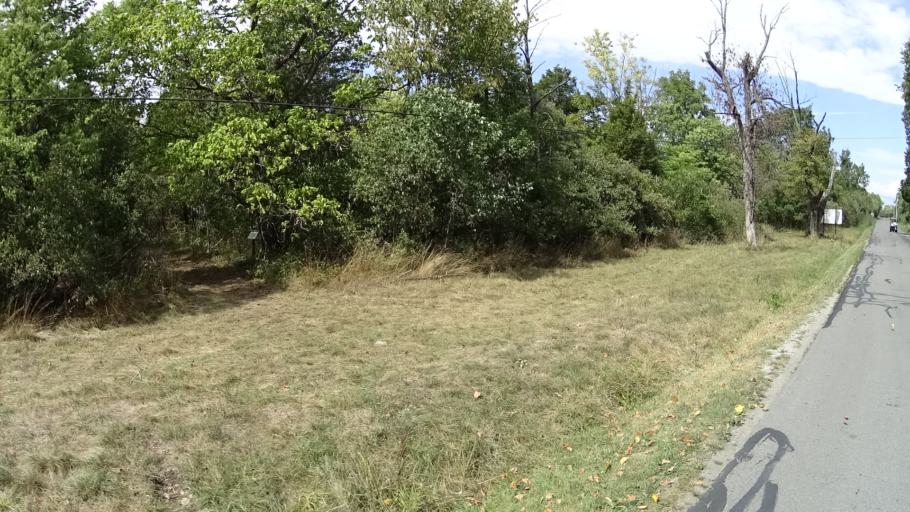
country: US
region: Ohio
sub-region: Erie County
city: Sandusky
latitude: 41.6043
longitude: -82.6891
